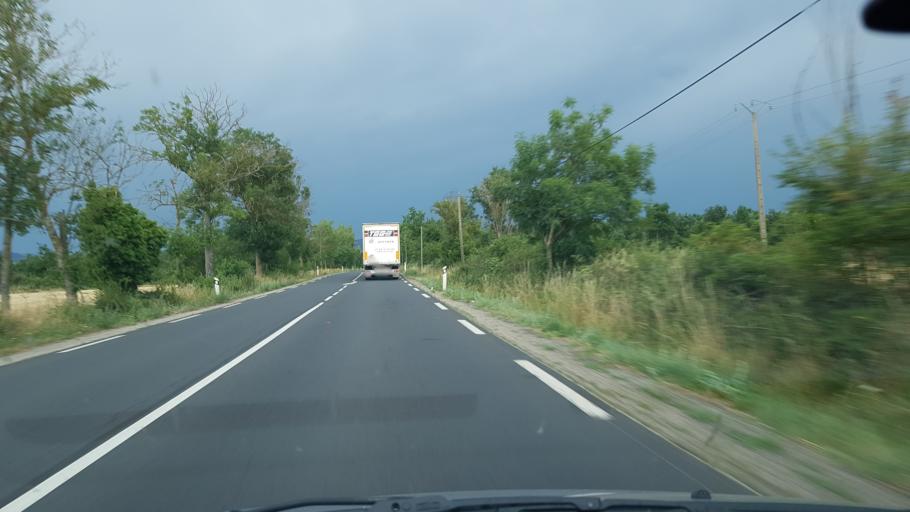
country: FR
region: Auvergne
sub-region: Departement de la Haute-Loire
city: Paulhaguet
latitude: 45.1640
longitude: 3.5328
